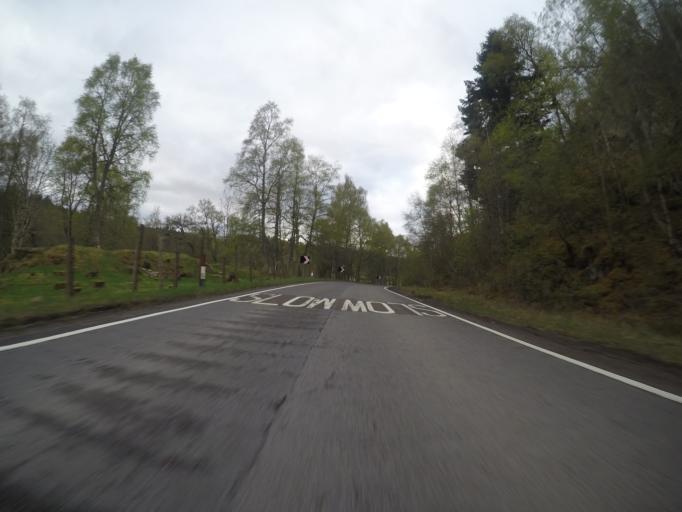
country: GB
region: Scotland
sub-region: Highland
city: Kingussie
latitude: 56.9760
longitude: -4.3811
